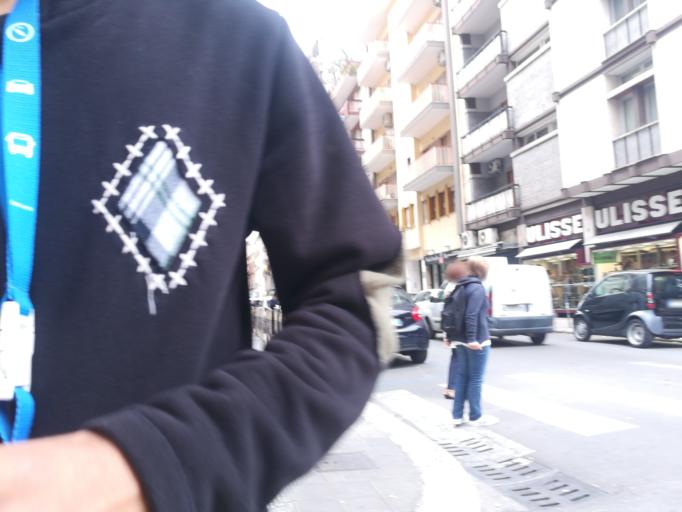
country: IT
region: Apulia
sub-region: Provincia di Bari
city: Bari
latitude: 41.1215
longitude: 16.8724
